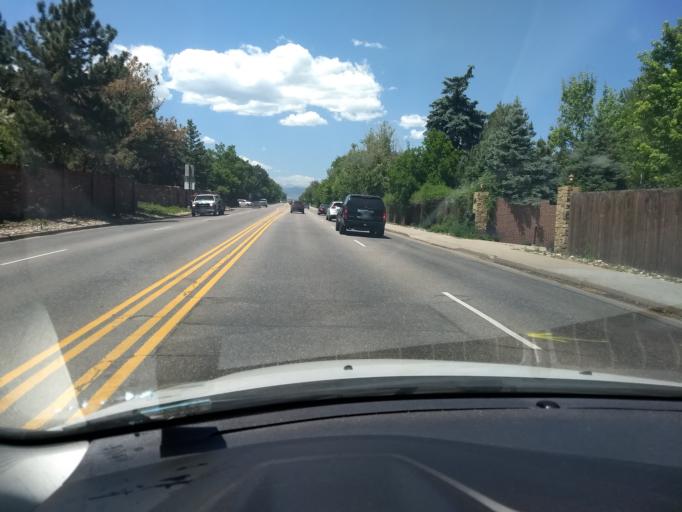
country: US
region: Colorado
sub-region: Arapahoe County
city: Cherry Hills Village
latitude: 39.6241
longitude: -104.9715
